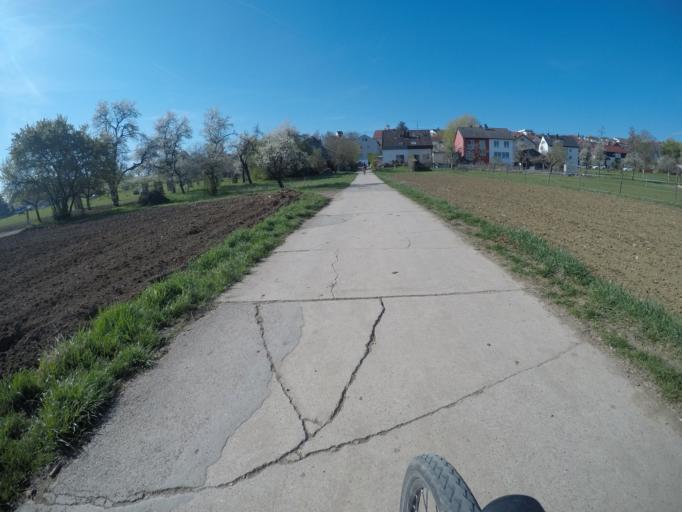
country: DE
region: Baden-Wuerttemberg
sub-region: Regierungsbezirk Stuttgart
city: Leinfelden-Echterdingen
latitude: 48.6732
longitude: 9.1724
